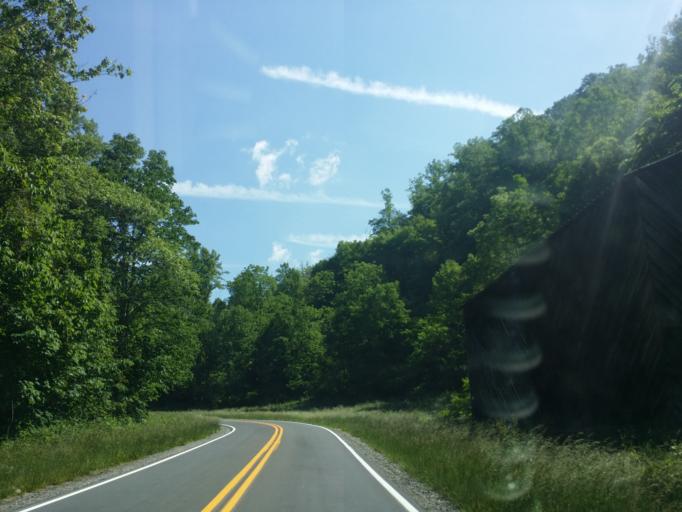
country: US
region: North Carolina
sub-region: Madison County
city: Marshall
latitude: 35.7385
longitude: -82.8491
